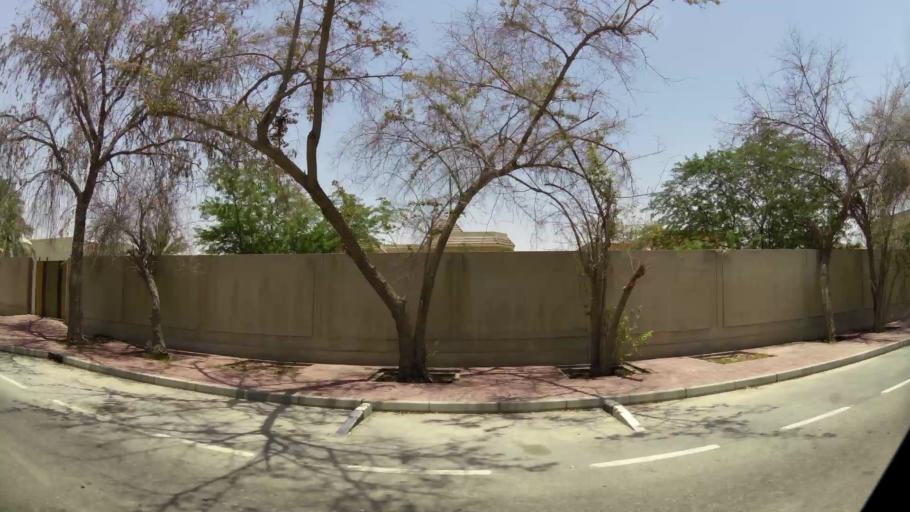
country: AE
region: Dubai
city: Dubai
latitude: 25.1791
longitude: 55.2323
